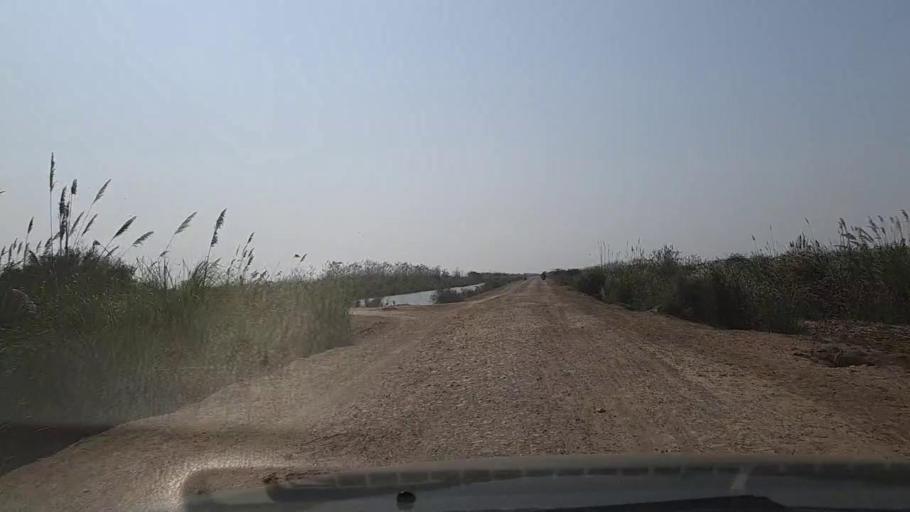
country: PK
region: Sindh
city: Mirpur Sakro
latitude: 24.3793
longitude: 67.6593
